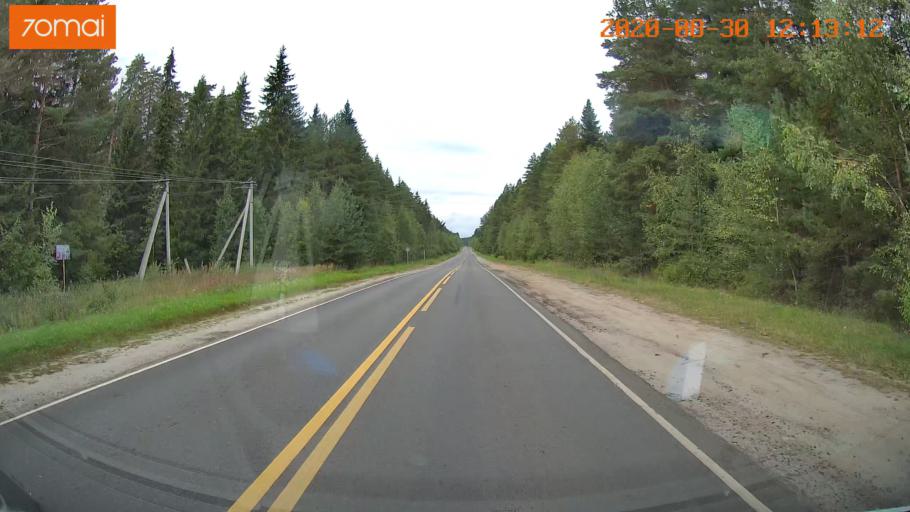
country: RU
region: Ivanovo
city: Yur'yevets
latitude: 57.3124
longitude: 43.0833
